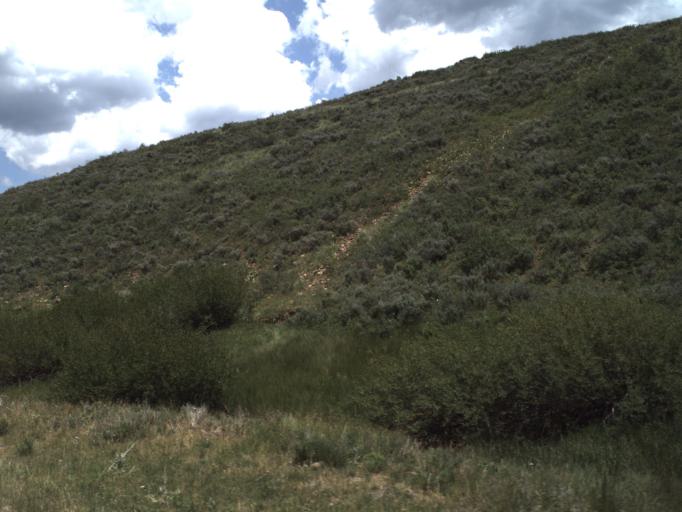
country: US
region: Utah
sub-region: Weber County
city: Wolf Creek
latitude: 41.4037
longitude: -111.5987
